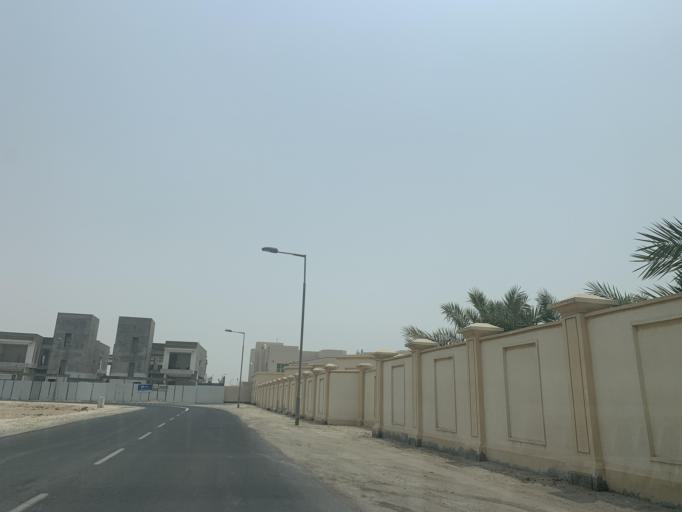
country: BH
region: Central Governorate
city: Madinat Hamad
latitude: 26.1707
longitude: 50.4804
